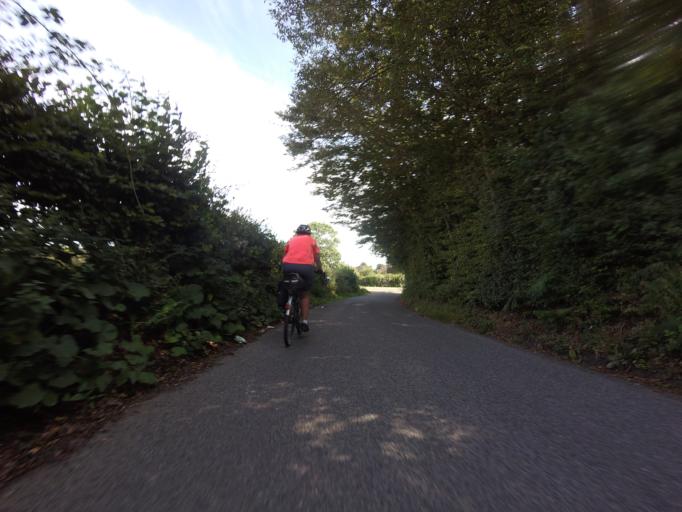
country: GB
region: England
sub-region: East Sussex
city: Rye
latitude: 50.9727
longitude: 0.7076
